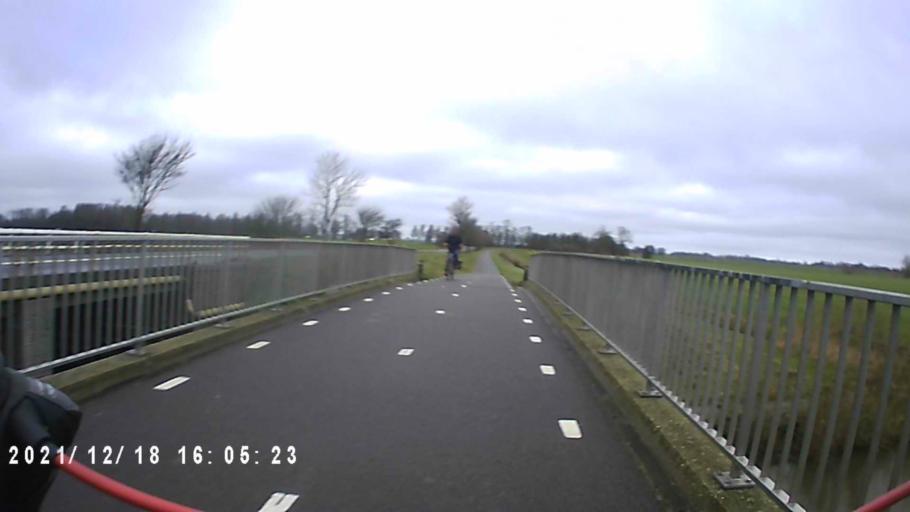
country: NL
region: Friesland
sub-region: Gemeente Dongeradeel
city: Anjum
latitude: 53.3537
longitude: 6.0770
